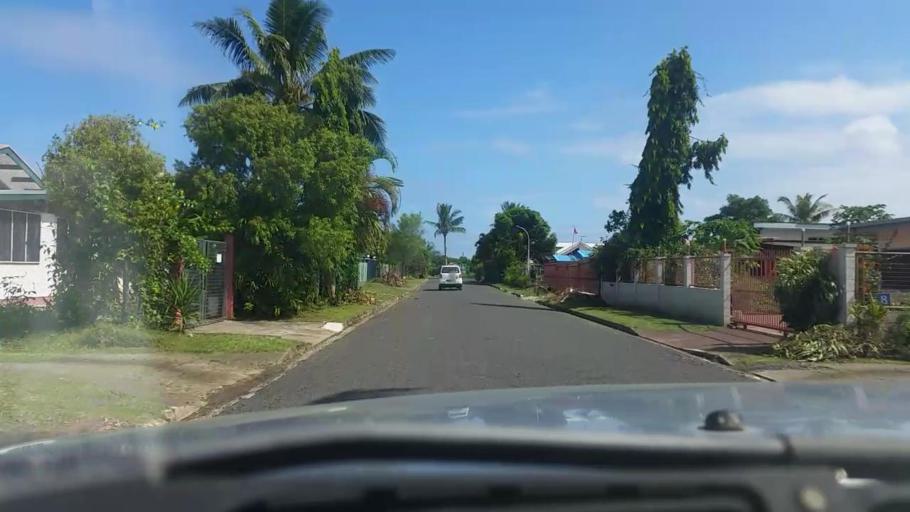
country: FJ
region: Central
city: Suva
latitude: -18.1309
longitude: 178.4651
